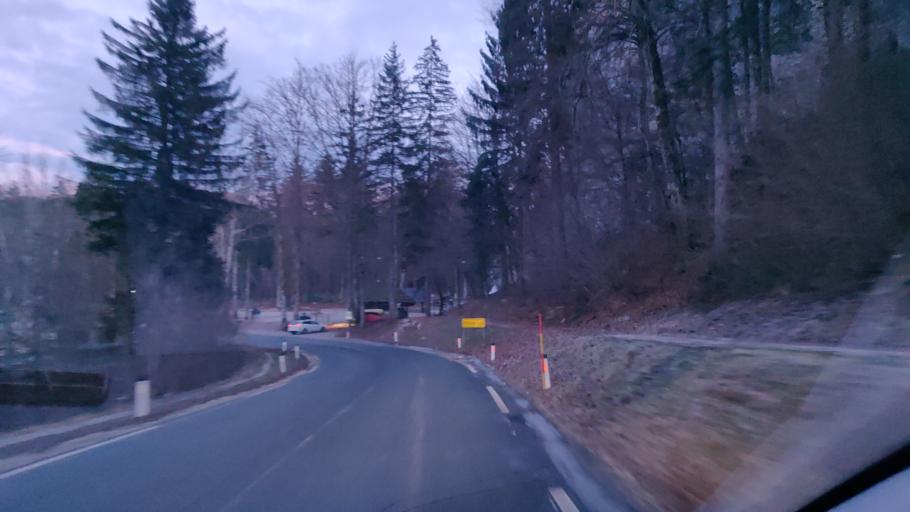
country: SI
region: Bohinj
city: Bohinjska Bistrica
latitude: 46.2762
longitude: 13.8826
